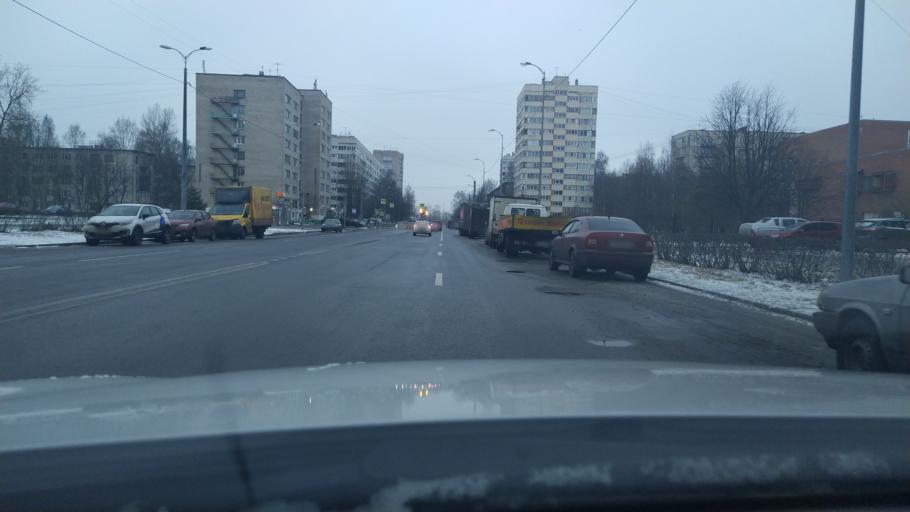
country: RU
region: St.-Petersburg
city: Grazhdanka
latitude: 60.0456
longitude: 30.3892
